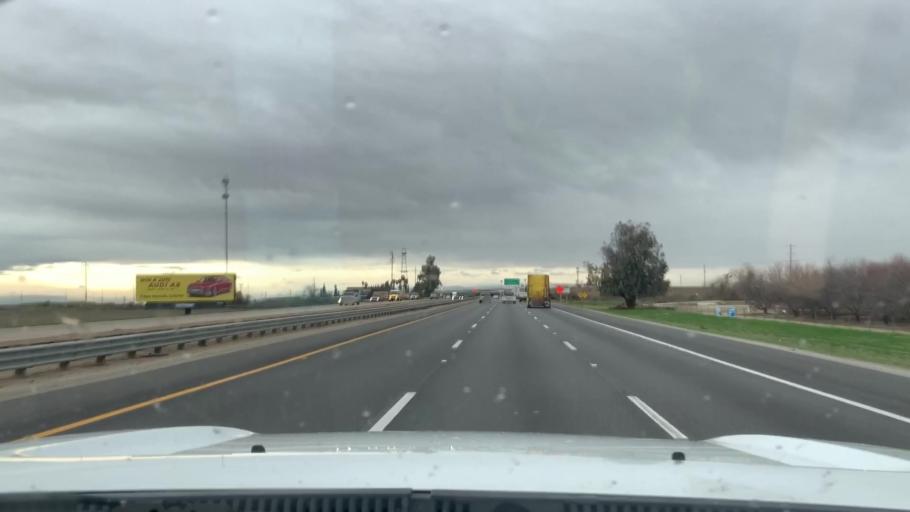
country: US
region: California
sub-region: Kern County
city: McFarland
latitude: 35.6083
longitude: -119.2120
